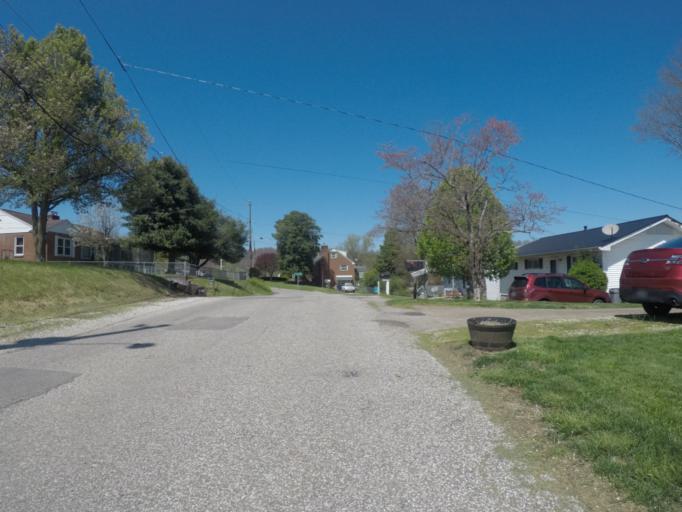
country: US
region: West Virginia
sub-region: Cabell County
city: Pea Ridge
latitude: 38.4200
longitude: -82.3068
